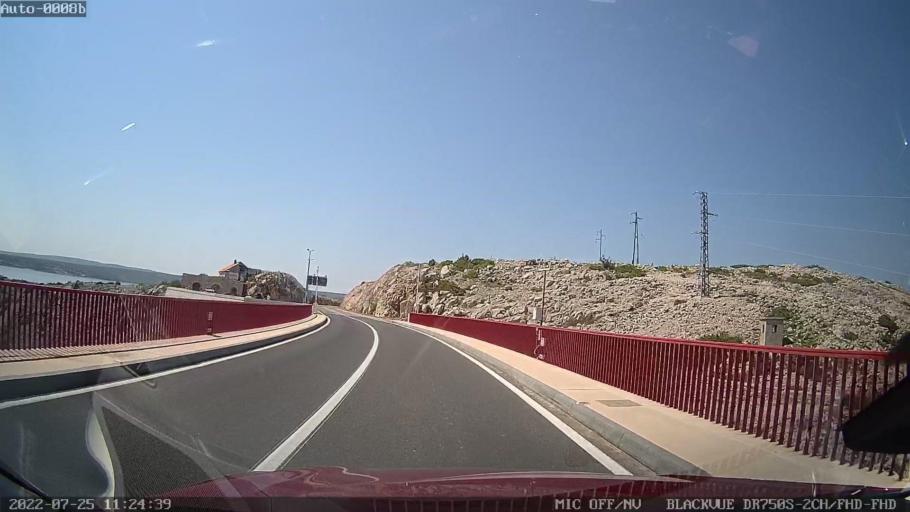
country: HR
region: Zadarska
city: Posedarje
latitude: 44.2241
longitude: 15.5298
